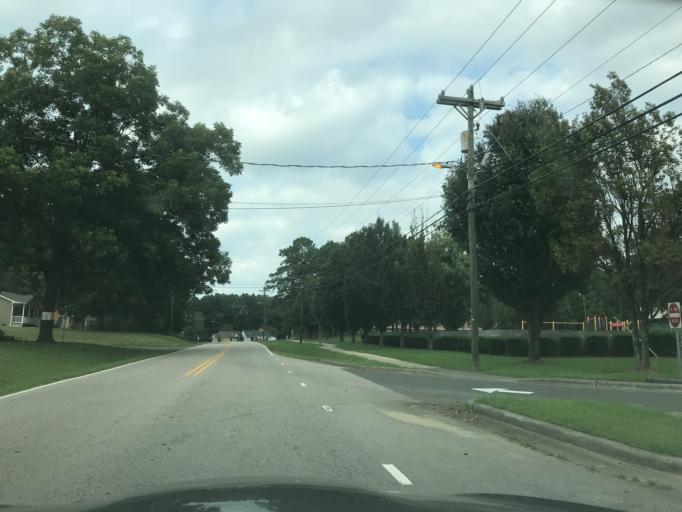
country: US
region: North Carolina
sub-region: Durham County
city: Durham
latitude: 35.9327
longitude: -78.9091
